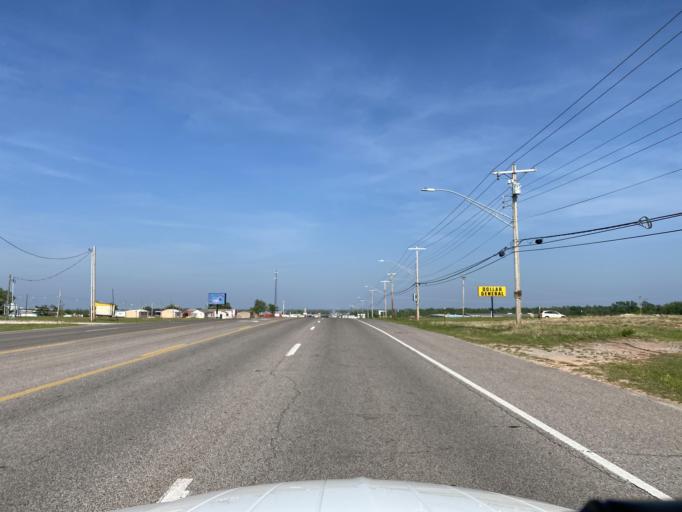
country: US
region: Oklahoma
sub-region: Oklahoma County
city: Nicoma Park
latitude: 35.4930
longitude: -97.3443
